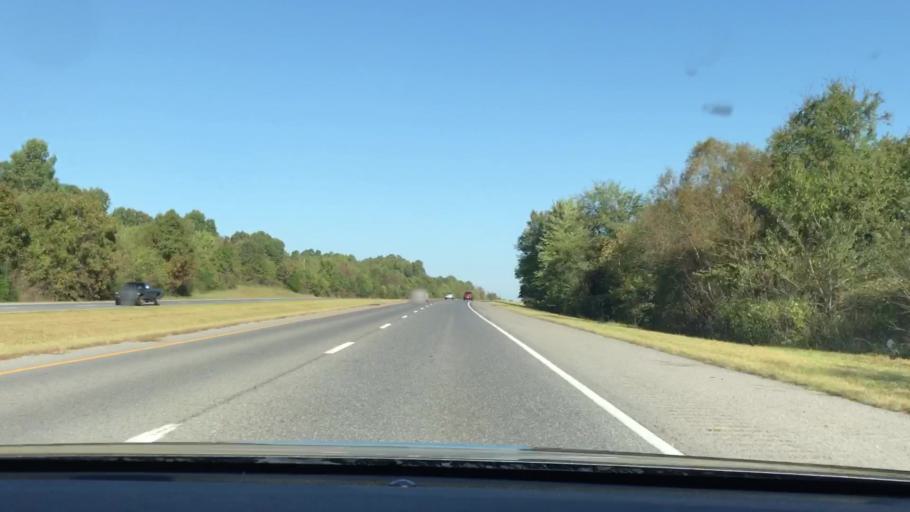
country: US
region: Kentucky
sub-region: Marshall County
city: Benton
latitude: 36.7768
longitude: -88.3203
